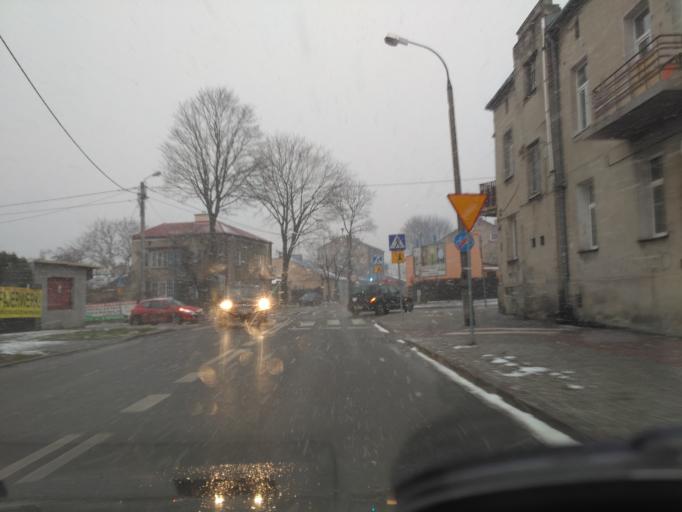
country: PL
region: Lublin Voivodeship
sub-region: Powiat lubelski
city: Lublin
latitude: 51.2284
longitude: 22.5814
